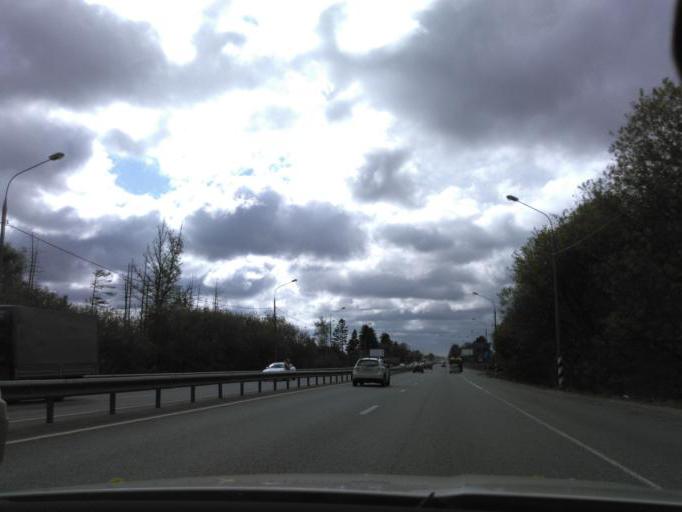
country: RU
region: Moskovskaya
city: Novopodrezkovo
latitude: 55.9666
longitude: 37.3264
